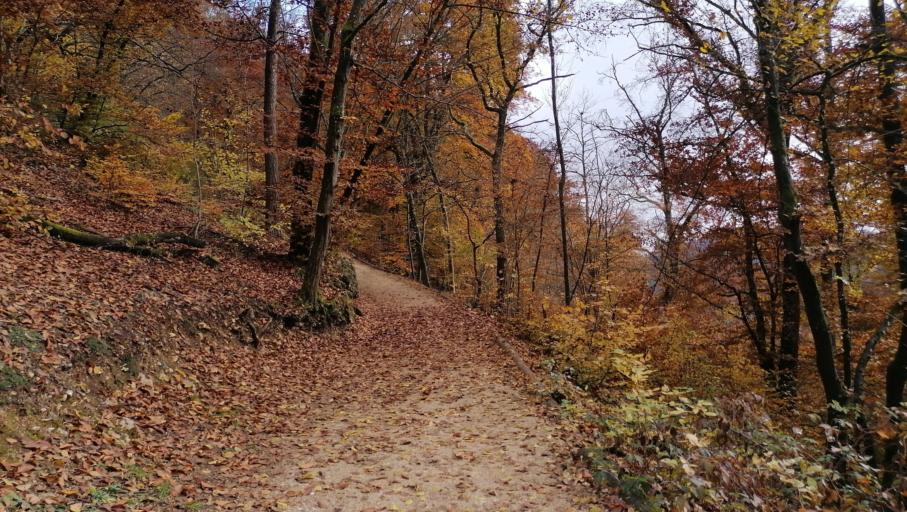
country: DE
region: Bavaria
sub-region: Lower Bavaria
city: Essing
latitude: 48.9287
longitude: 11.8168
